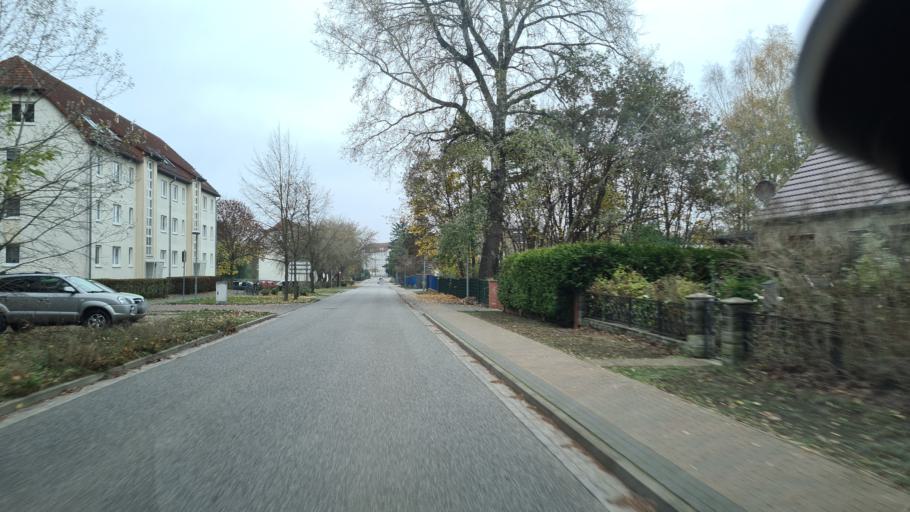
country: DE
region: Brandenburg
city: Lindow
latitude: 52.9637
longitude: 12.9911
